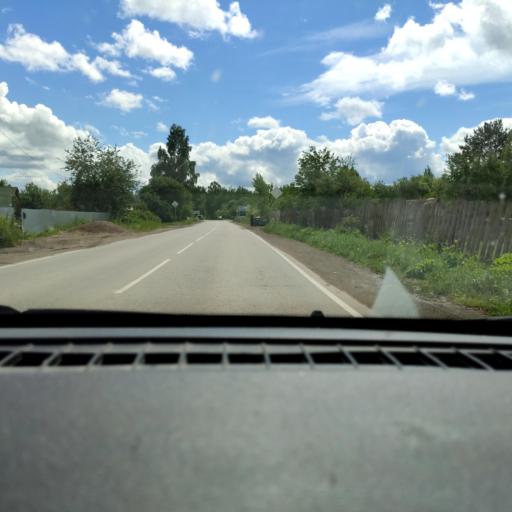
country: RU
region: Perm
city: Overyata
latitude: 58.1151
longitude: 55.8329
